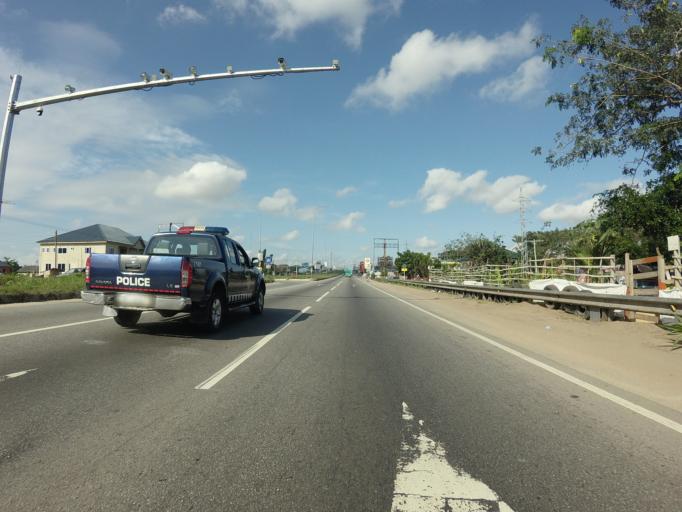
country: GH
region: Central
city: Kasoa
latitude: 5.5458
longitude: -0.3846
